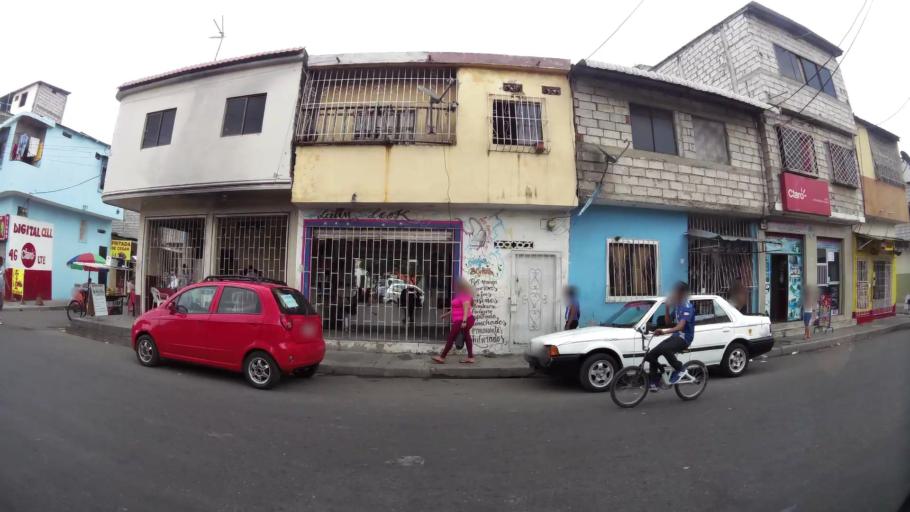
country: EC
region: Guayas
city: Guayaquil
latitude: -2.2297
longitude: -79.9112
